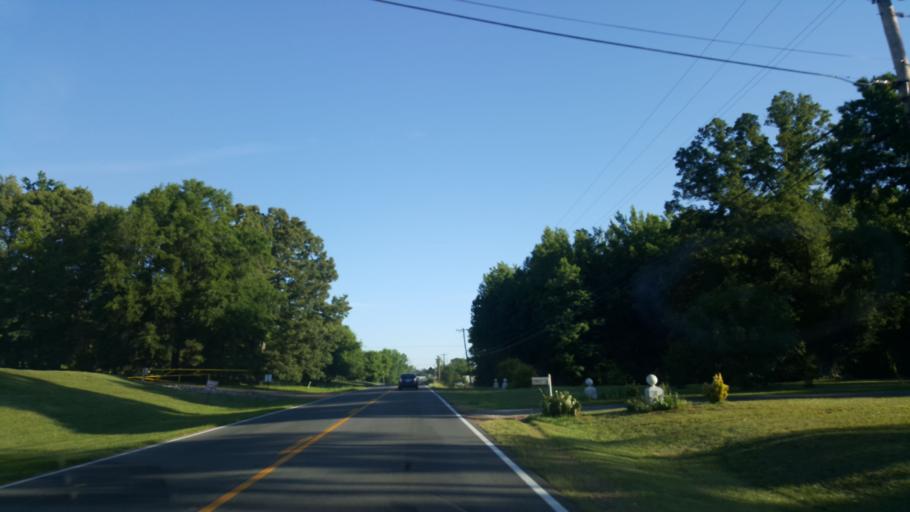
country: US
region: Tennessee
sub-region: Henderson County
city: Lexington
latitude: 35.6159
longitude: -88.4018
